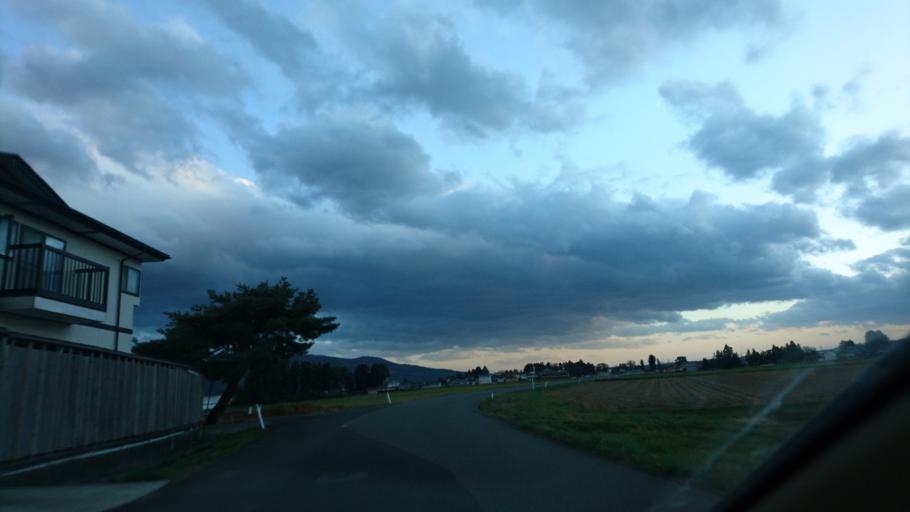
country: JP
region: Iwate
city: Mizusawa
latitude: 39.0717
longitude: 141.1413
